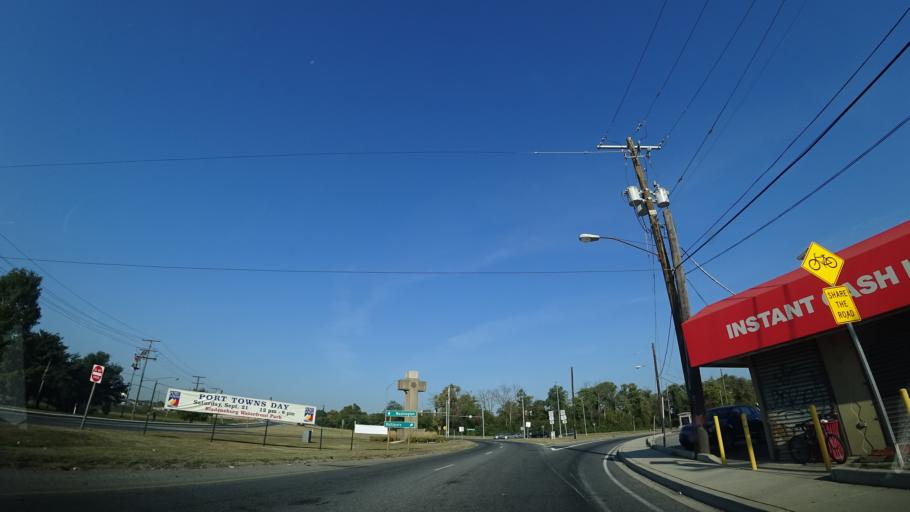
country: US
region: Maryland
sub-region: Prince George's County
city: Bladensburg
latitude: 38.9393
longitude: -76.9400
